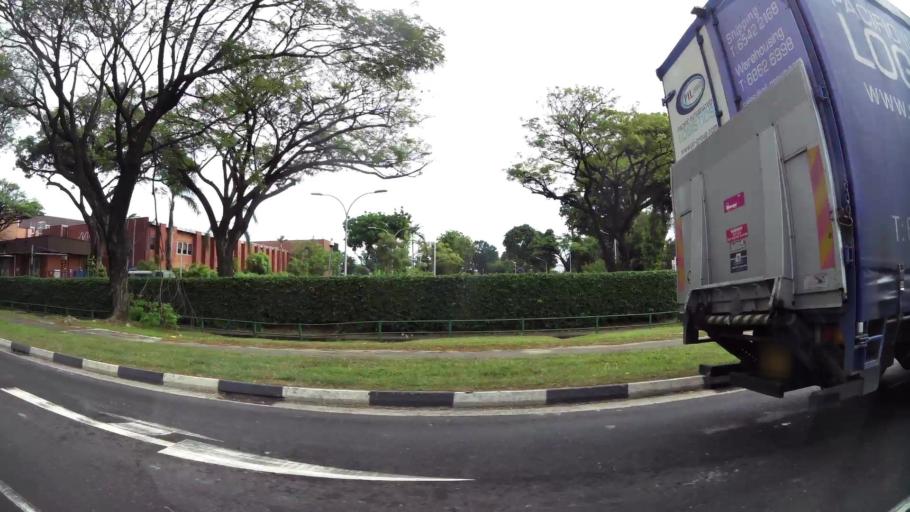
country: MY
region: Johor
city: Johor Bahru
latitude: 1.3104
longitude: 103.6603
